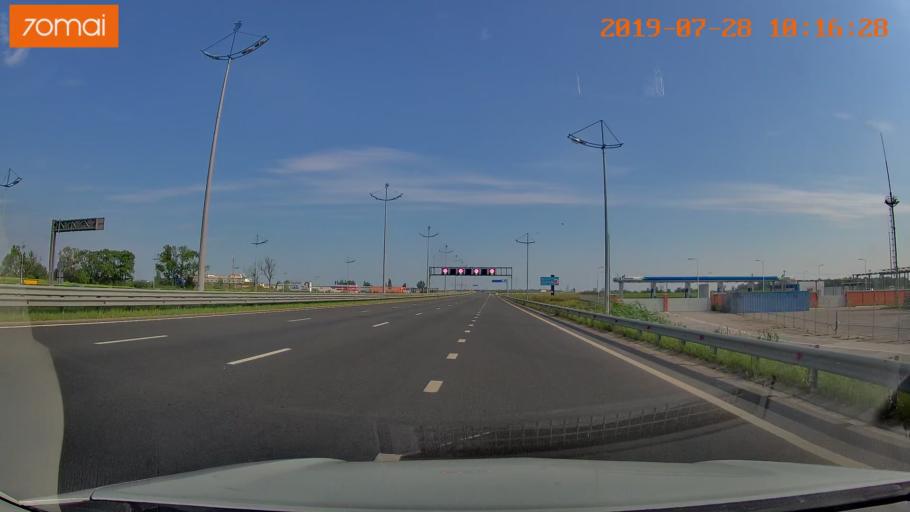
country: RU
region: Kaliningrad
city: Bol'shoe Isakovo
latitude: 54.7269
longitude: 20.5975
